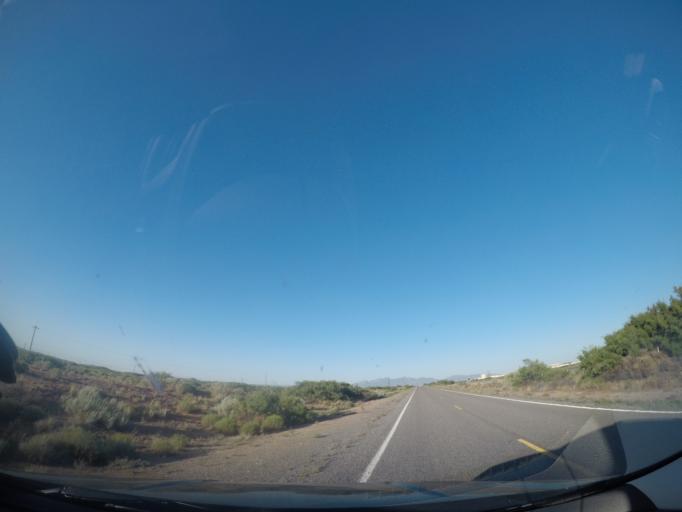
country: US
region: New Mexico
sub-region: Dona Ana County
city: Mesilla
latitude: 32.2697
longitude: -106.9472
